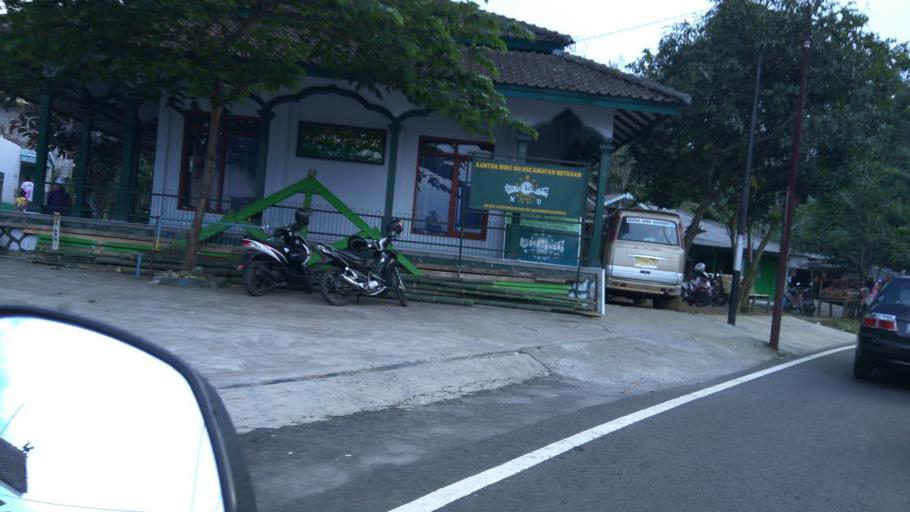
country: ID
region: Central Java
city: Gunung Kendil
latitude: -7.3732
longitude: 110.4458
